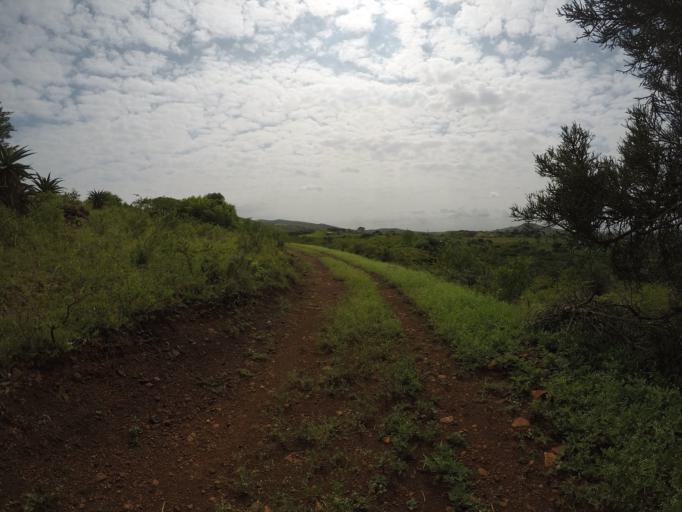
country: ZA
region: KwaZulu-Natal
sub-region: uThungulu District Municipality
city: Empangeni
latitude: -28.6187
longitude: 31.8987
